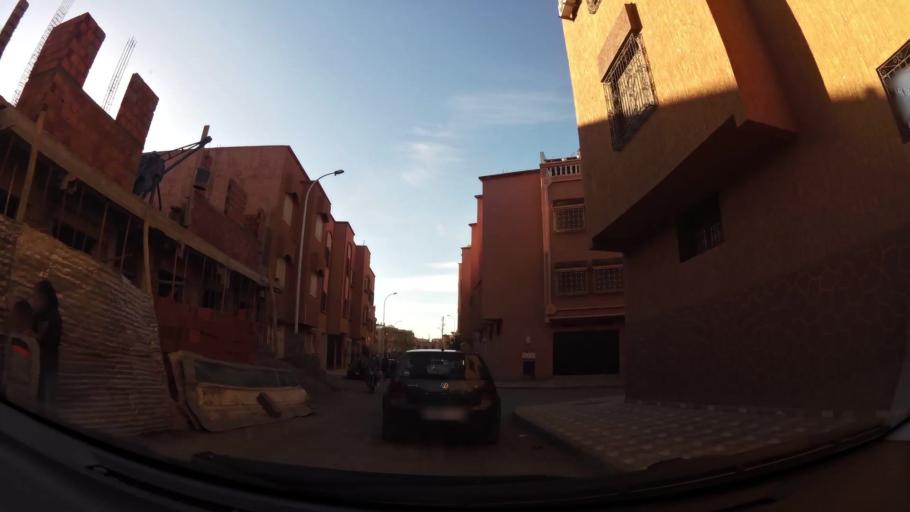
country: MA
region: Marrakech-Tensift-Al Haouz
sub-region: Marrakech
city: Marrakesh
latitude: 31.6181
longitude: -8.0597
